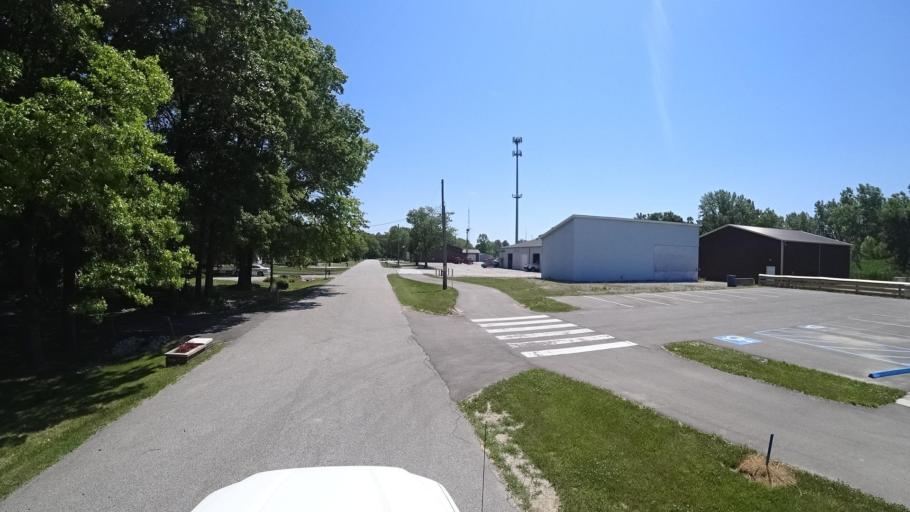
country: US
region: Indiana
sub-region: Porter County
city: Burns Harbor
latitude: 41.6128
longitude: -87.1292
